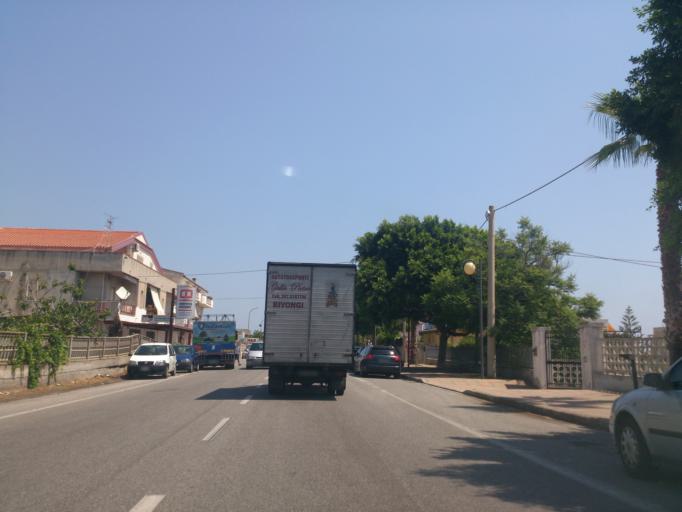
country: IT
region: Calabria
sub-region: Provincia di Reggio Calabria
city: Riace Marina
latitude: 38.3906
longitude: 16.5304
